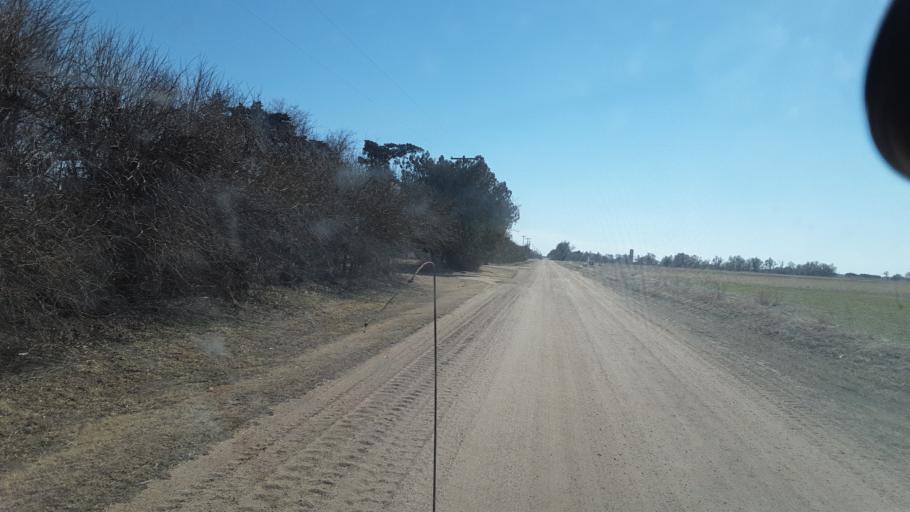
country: US
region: Kansas
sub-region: Reno County
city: South Hutchinson
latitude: 38.0025
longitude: -97.9955
